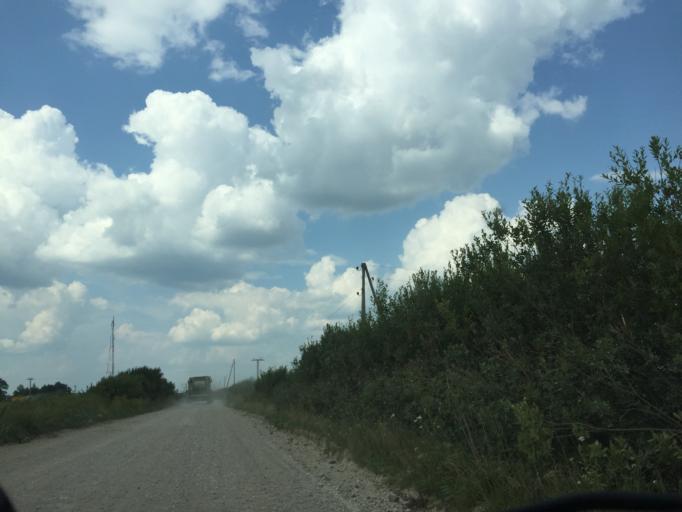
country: LT
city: Naujoji Akmene
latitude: 56.3488
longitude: 23.0597
